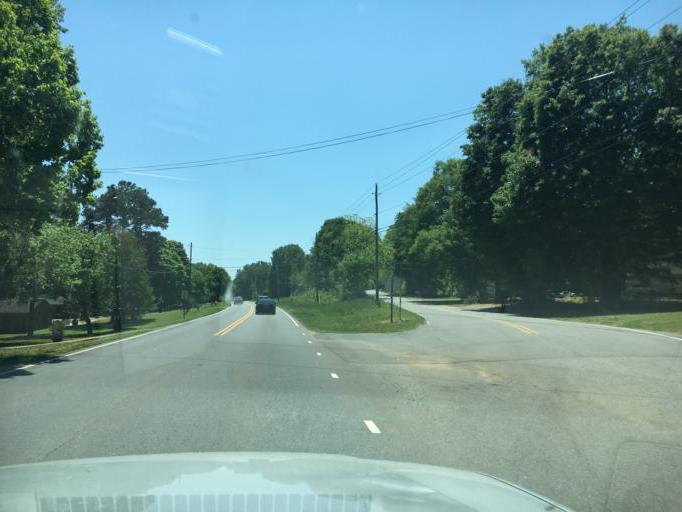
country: US
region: North Carolina
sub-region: Cleveland County
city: Shelby
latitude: 35.2526
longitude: -81.5659
